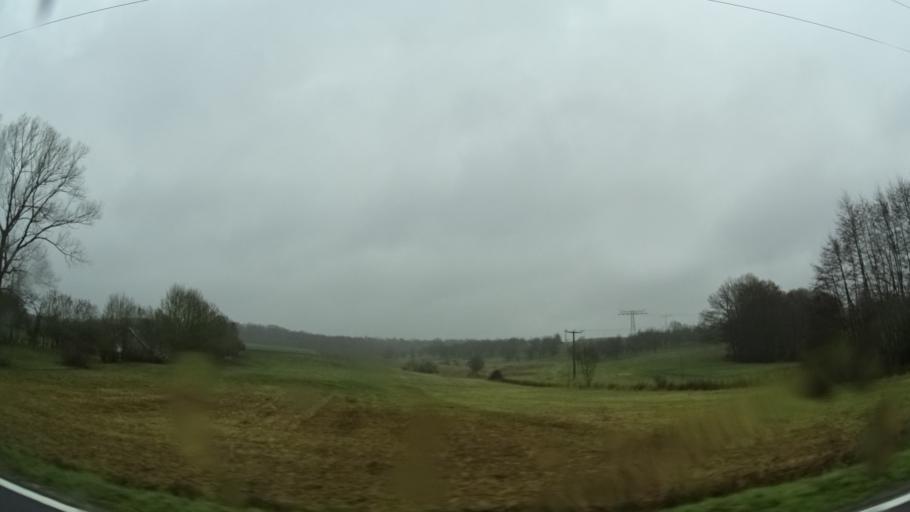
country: DE
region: Thuringia
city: Gleichamberg
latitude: 50.3919
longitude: 10.6425
